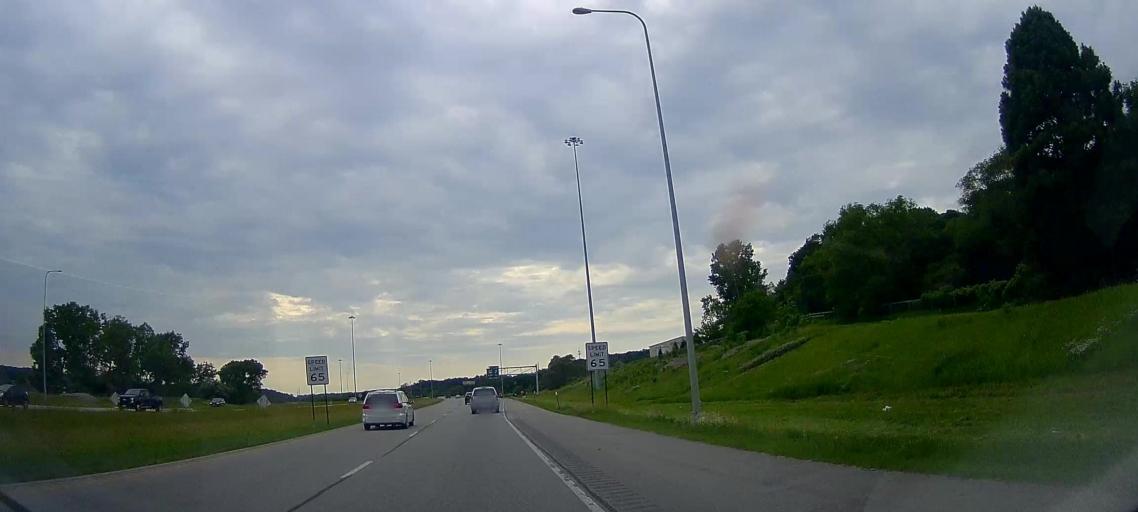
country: US
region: Iowa
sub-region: Pottawattamie County
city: Carter Lake
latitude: 41.3465
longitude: -95.9763
